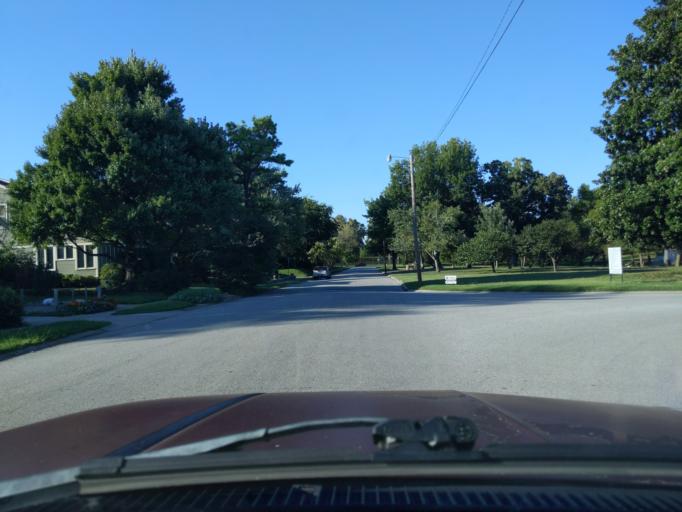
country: US
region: Oklahoma
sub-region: Tulsa County
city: Tulsa
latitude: 36.1594
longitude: -96.0071
